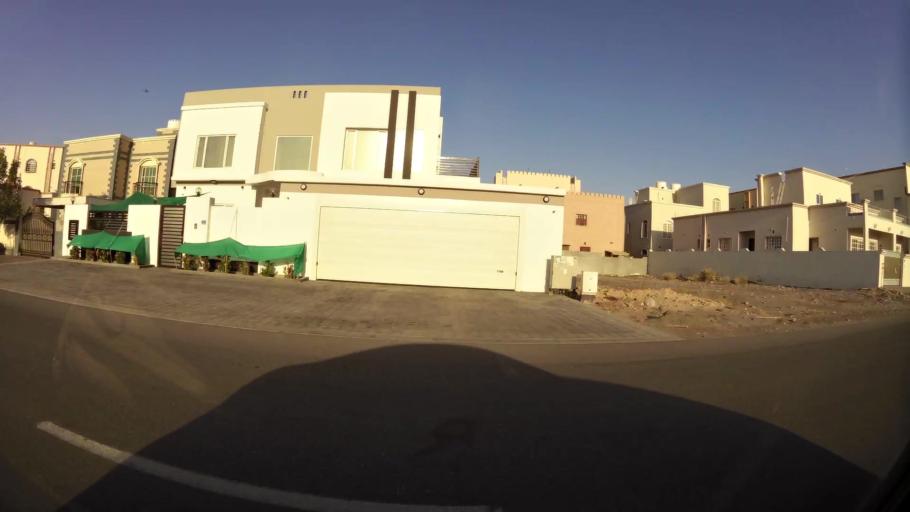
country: OM
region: Muhafazat Masqat
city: As Sib al Jadidah
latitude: 23.5925
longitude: 58.1382
